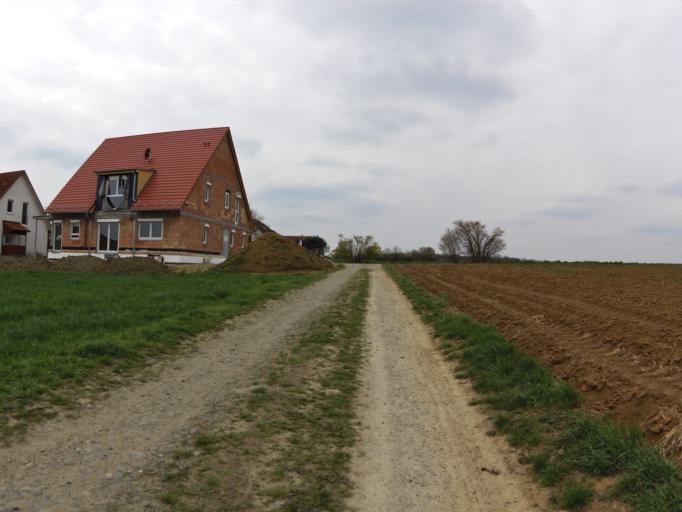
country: DE
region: Bavaria
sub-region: Regierungsbezirk Unterfranken
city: Rottendorf
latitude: 49.8006
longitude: 10.0261
